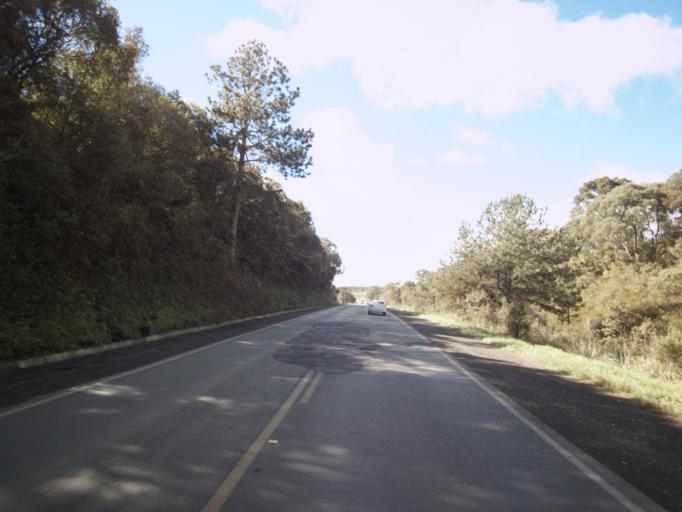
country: BR
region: Santa Catarina
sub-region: Concordia
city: Concordia
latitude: -26.9780
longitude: -51.8651
